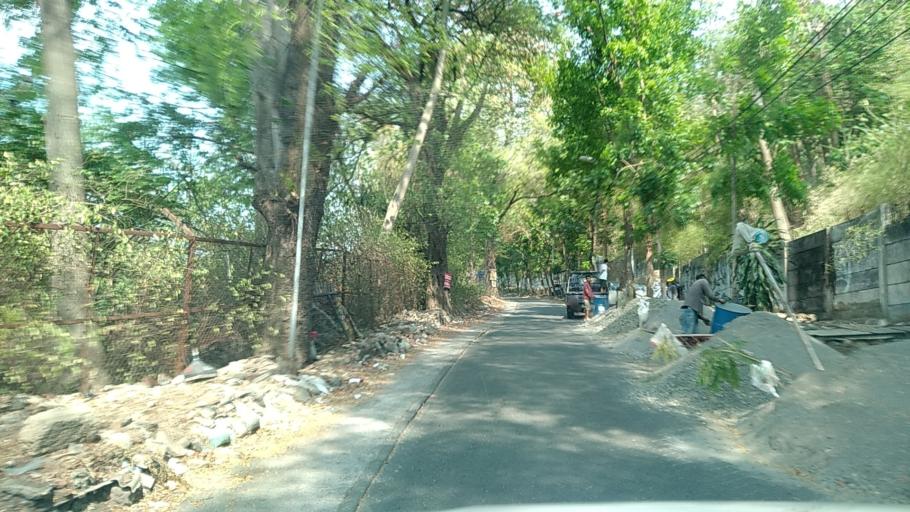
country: ID
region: Central Java
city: Semarang
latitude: -6.9913
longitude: 110.4069
